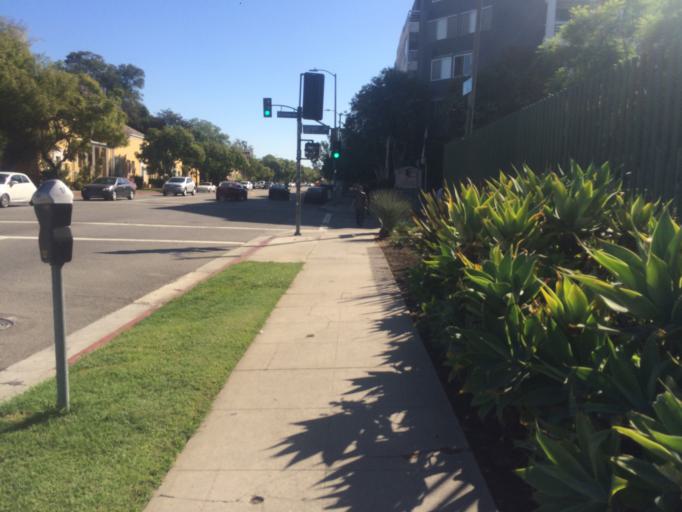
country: US
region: California
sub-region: Los Angeles County
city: West Hollywood
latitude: 34.0648
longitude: -118.3550
